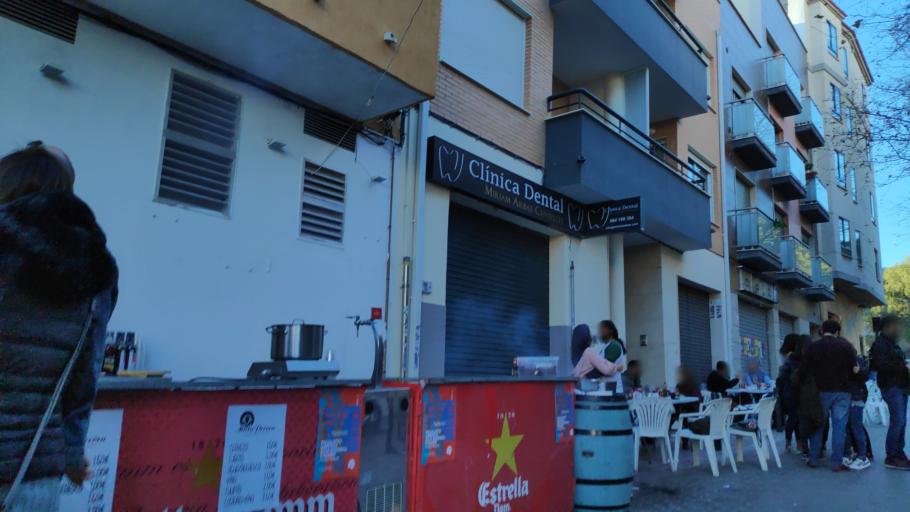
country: ES
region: Valencia
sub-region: Provincia de Castello
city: Benicassim
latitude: 40.0554
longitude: 0.0625
